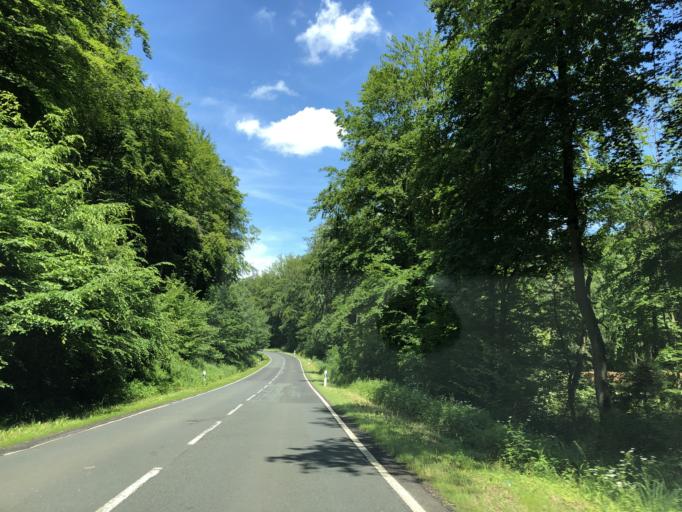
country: DE
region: Hesse
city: Wetter
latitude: 50.8442
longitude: 8.6830
